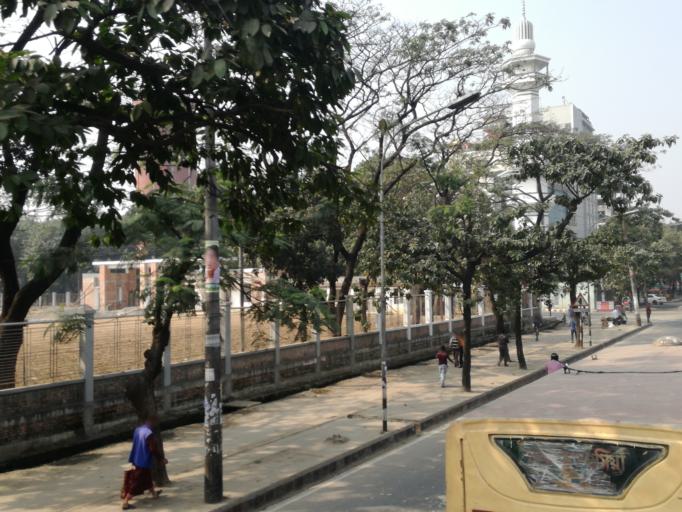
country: BD
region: Dhaka
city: Tungi
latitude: 23.8542
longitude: 90.4052
